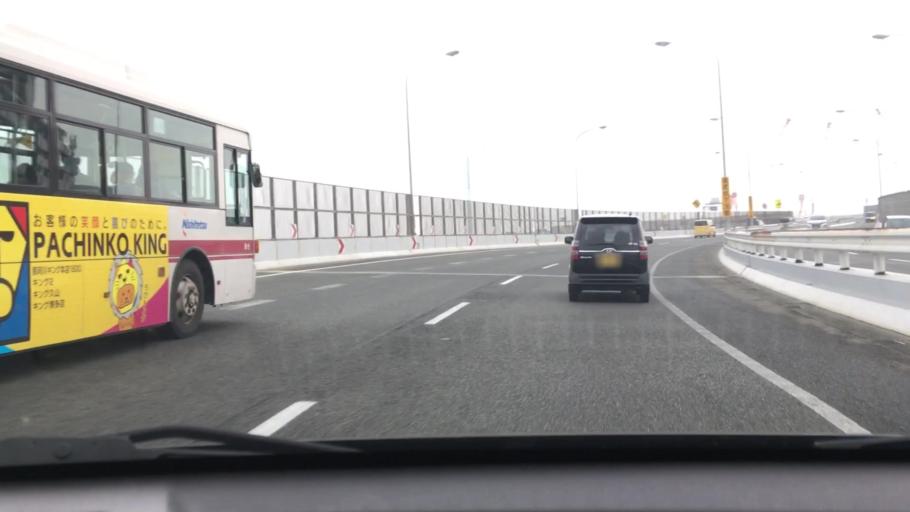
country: JP
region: Fukuoka
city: Fukuoka-shi
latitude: 33.6001
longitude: 130.3769
